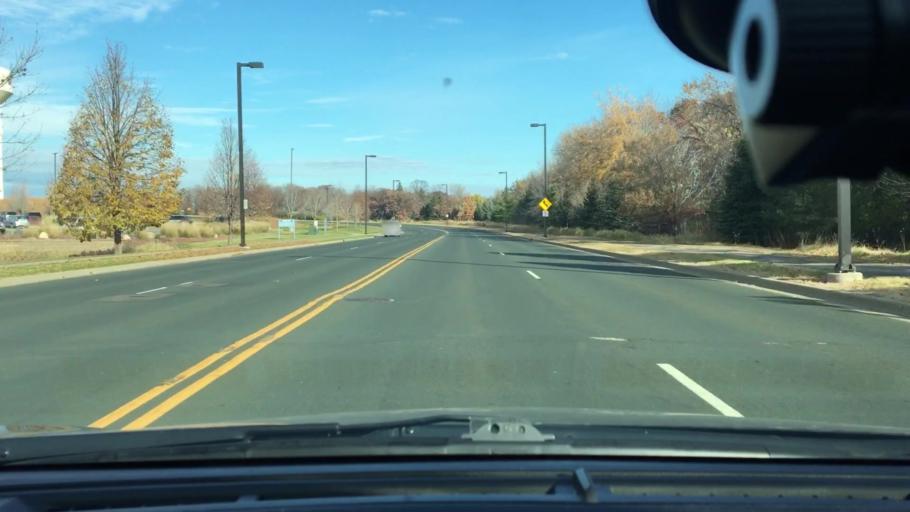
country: US
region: Minnesota
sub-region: Hennepin County
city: Maple Grove
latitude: 45.0755
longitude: -93.4417
